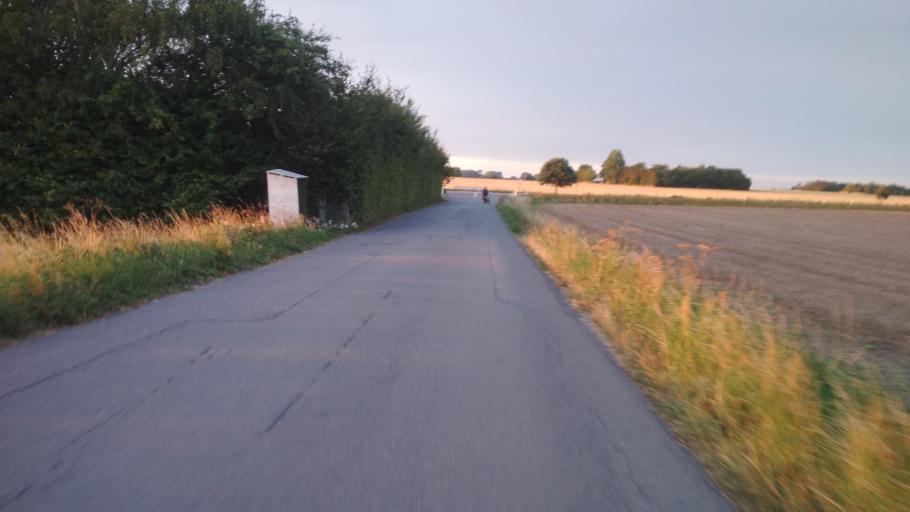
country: DK
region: Capital Region
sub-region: Bornholm Kommune
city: Akirkeby
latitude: 55.0338
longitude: 14.9156
